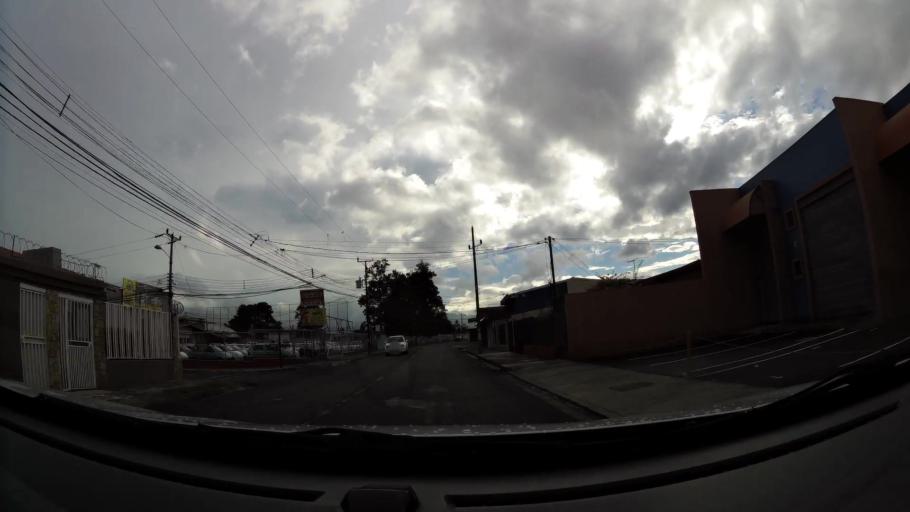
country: CR
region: San Jose
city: Colima
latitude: 9.9420
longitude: -84.0925
